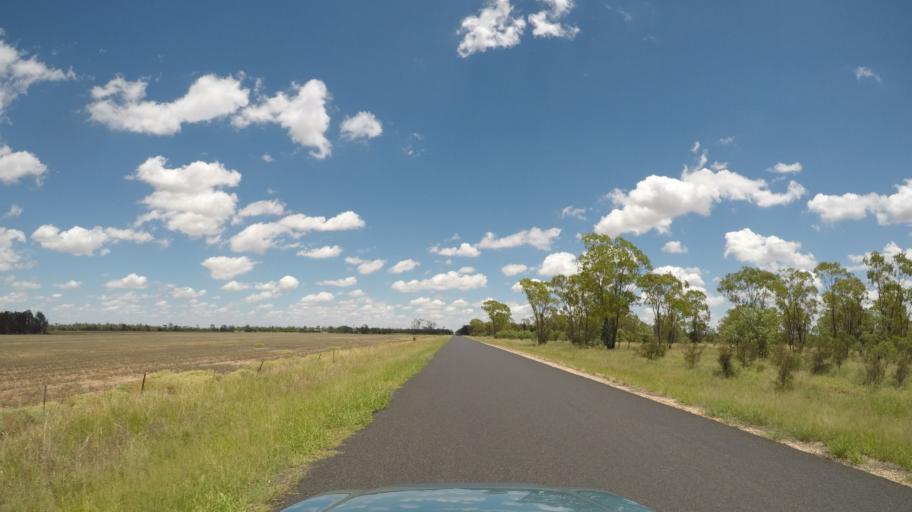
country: AU
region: Queensland
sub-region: Goondiwindi
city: Goondiwindi
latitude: -28.1692
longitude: 150.4613
